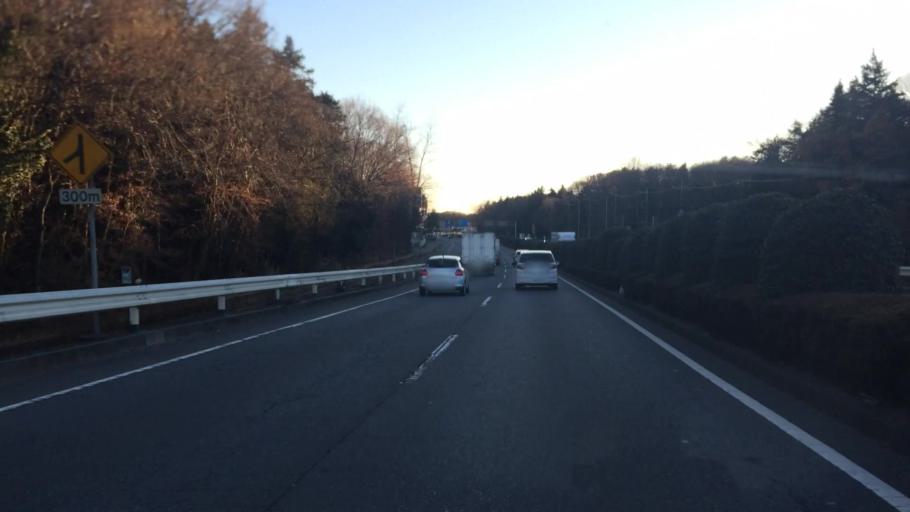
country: JP
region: Tochigi
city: Utsunomiya-shi
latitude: 36.5212
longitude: 139.9200
